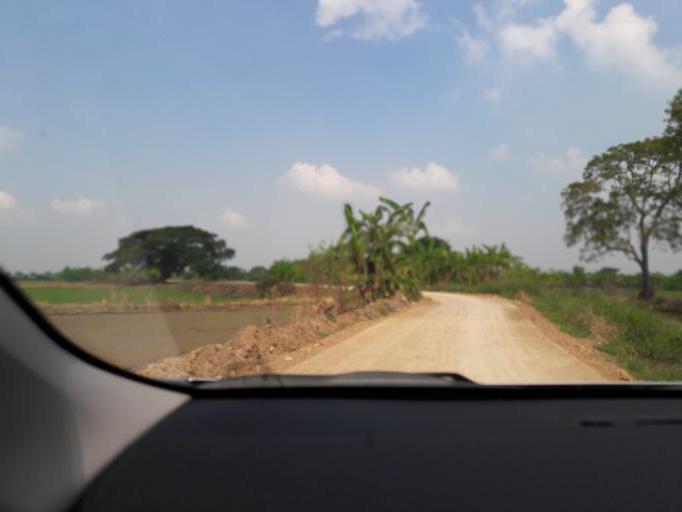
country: TH
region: Ang Thong
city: Ang Thong
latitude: 14.5614
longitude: 100.4177
